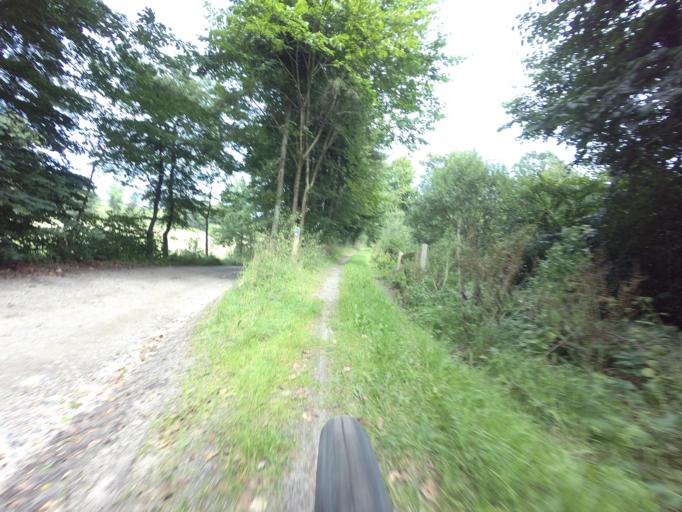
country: DK
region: Central Jutland
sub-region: Syddjurs Kommune
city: Ryomgard
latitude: 56.4003
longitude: 10.5332
